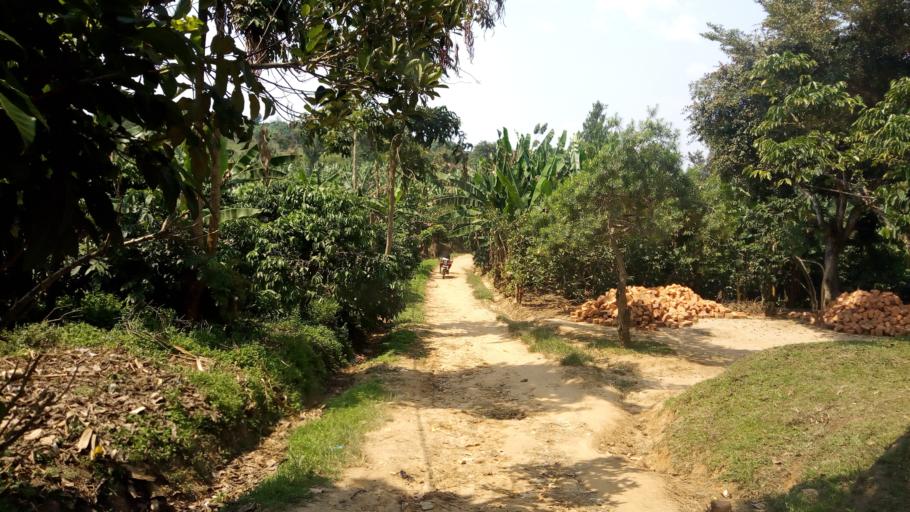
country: UG
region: Western Region
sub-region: Kanungu District
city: Ntungamo
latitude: -0.8065
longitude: 29.6453
